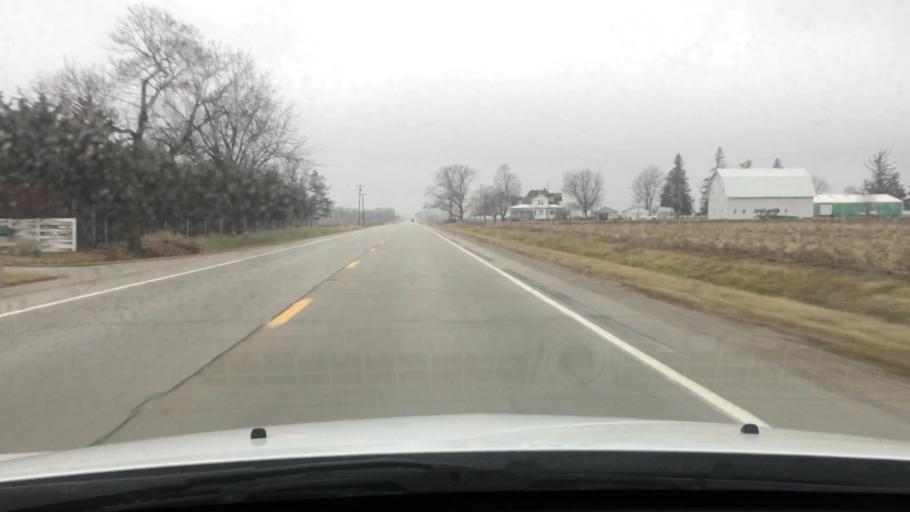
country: US
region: Illinois
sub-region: Livingston County
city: Flanagan
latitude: 40.8705
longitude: -88.8814
